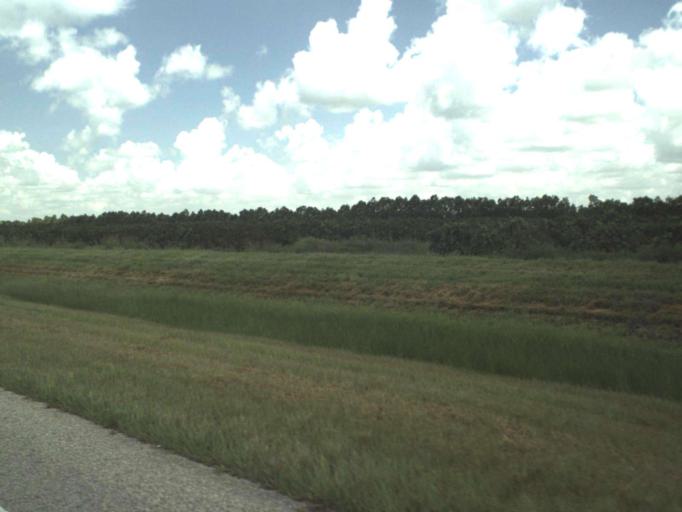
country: US
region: Florida
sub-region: Indian River County
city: West Vero Corridor
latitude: 27.6402
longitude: -80.6028
